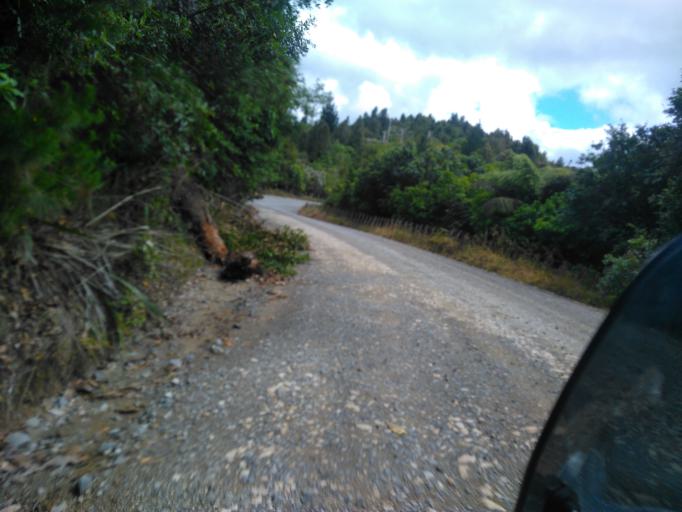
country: NZ
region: Gisborne
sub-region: Gisborne District
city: Gisborne
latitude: -38.2357
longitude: 178.0667
